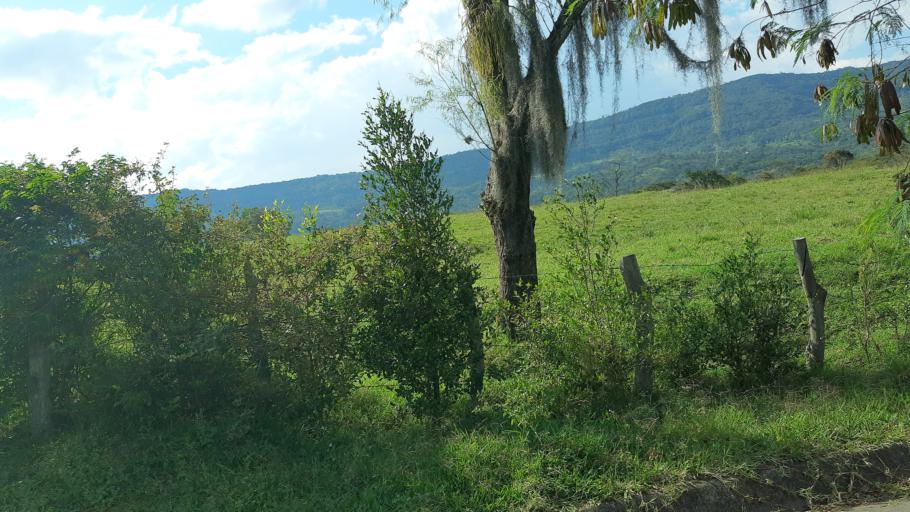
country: CO
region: Boyaca
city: Moniquira
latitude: 5.8307
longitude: -73.5914
